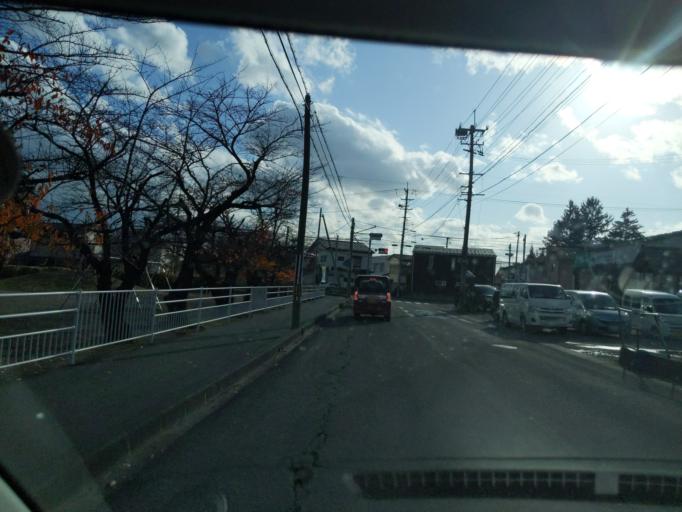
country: JP
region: Iwate
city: Mizusawa
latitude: 39.1393
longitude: 141.1567
